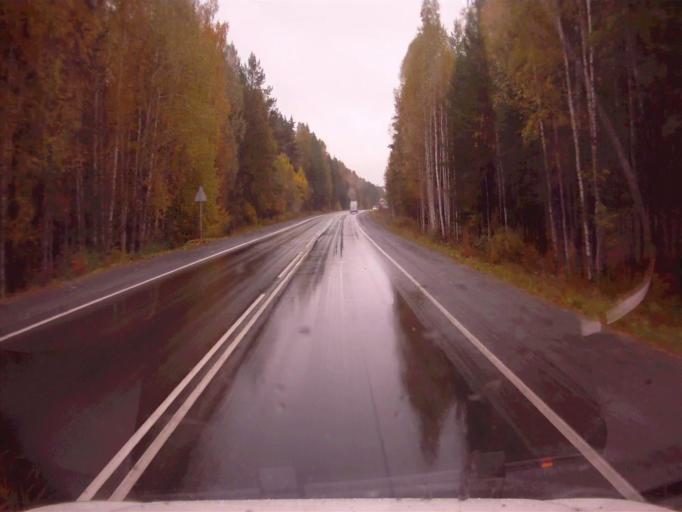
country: RU
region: Chelyabinsk
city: Tayginka
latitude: 55.5582
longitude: 60.6465
